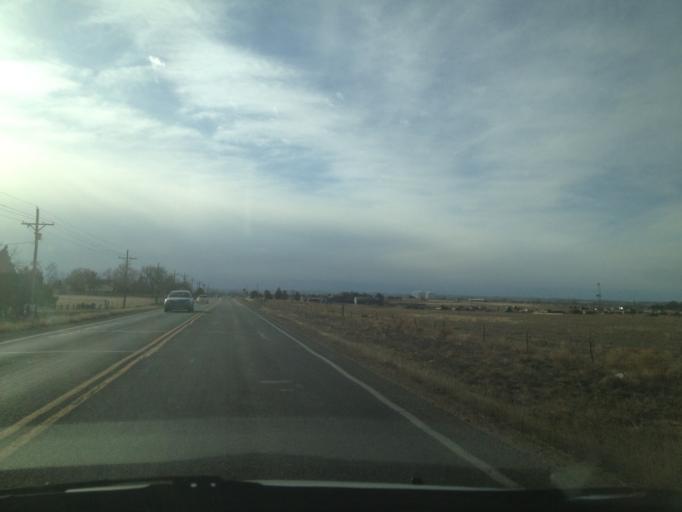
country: US
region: Colorado
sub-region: Weld County
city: Aristocrat Ranchettes
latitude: 40.0803
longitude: -104.7671
